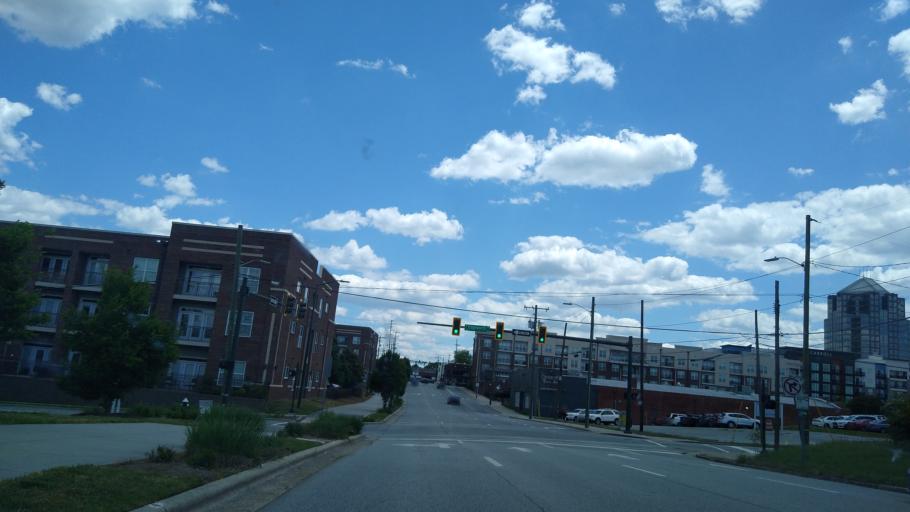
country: US
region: North Carolina
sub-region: Guilford County
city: Greensboro
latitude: 36.0783
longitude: -79.7962
